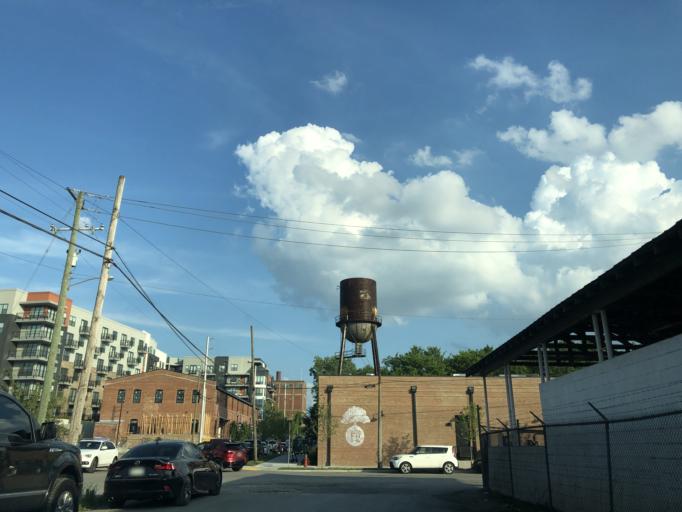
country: US
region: Tennessee
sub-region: Davidson County
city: Nashville
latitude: 36.1824
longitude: -86.7851
